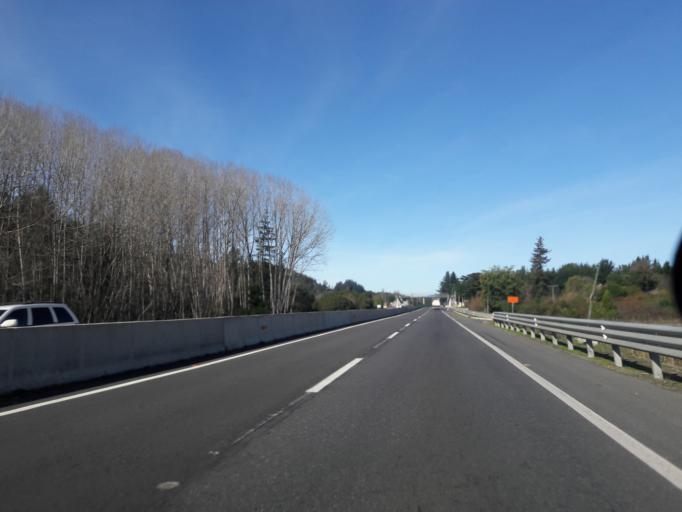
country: CL
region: Biobio
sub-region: Provincia de Biobio
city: Yumbel
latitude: -36.9481
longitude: -72.7513
